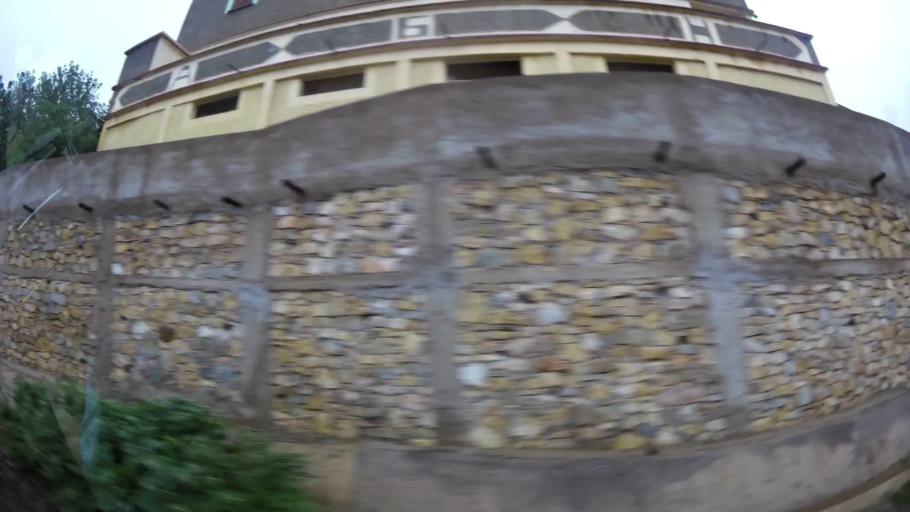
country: MA
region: Oriental
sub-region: Nador
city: Boudinar
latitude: 35.1309
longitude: -3.5890
